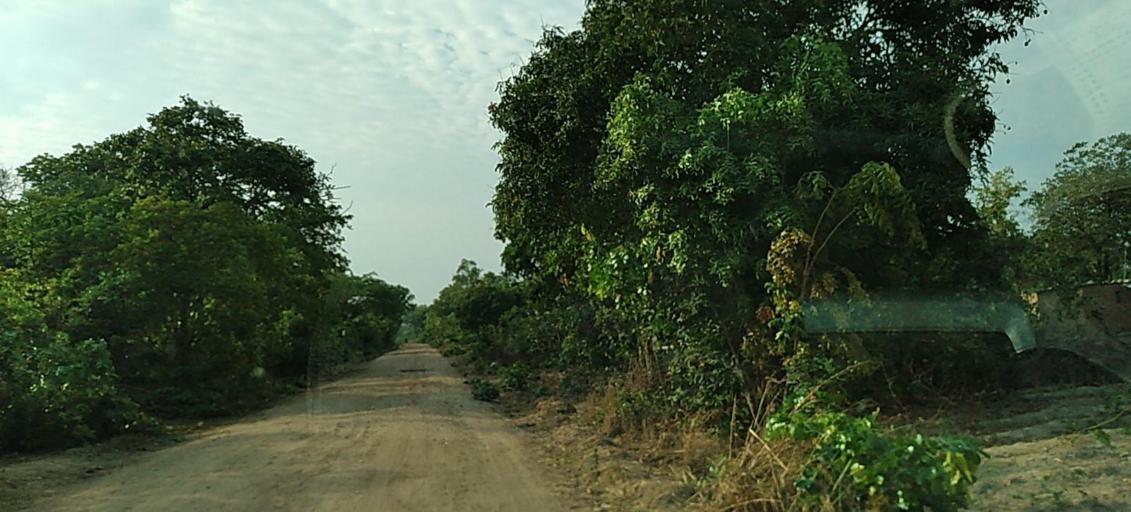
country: ZM
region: Copperbelt
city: Chingola
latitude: -12.8727
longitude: 27.6897
